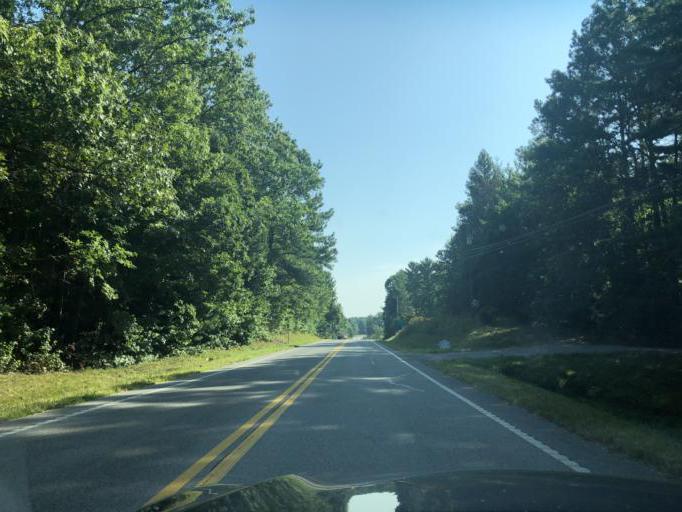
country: US
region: Tennessee
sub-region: Franklin County
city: Sewanee
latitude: 35.2190
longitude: -85.8829
